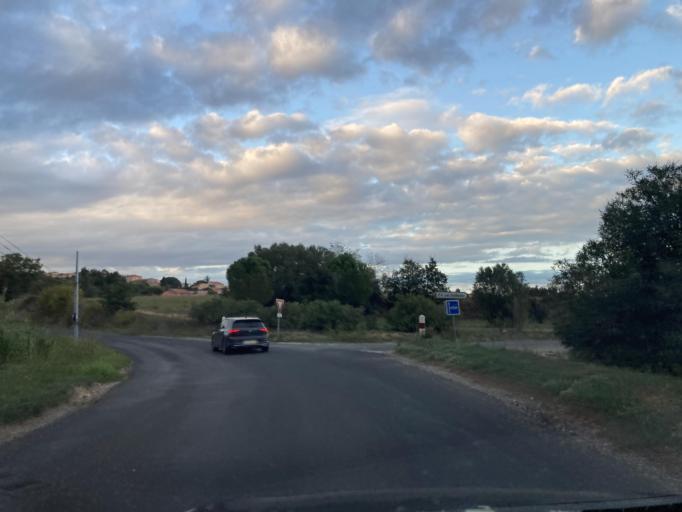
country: FR
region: Languedoc-Roussillon
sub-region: Departement des Pyrenees-Orientales
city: Banyuls-dels-Aspres
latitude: 42.5597
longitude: 2.8712
